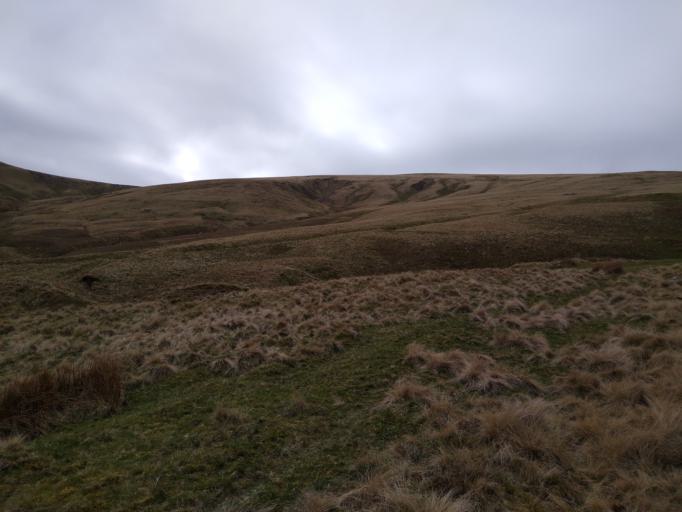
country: GB
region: England
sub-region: Cumbria
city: Keswick
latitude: 54.7057
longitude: -3.0419
